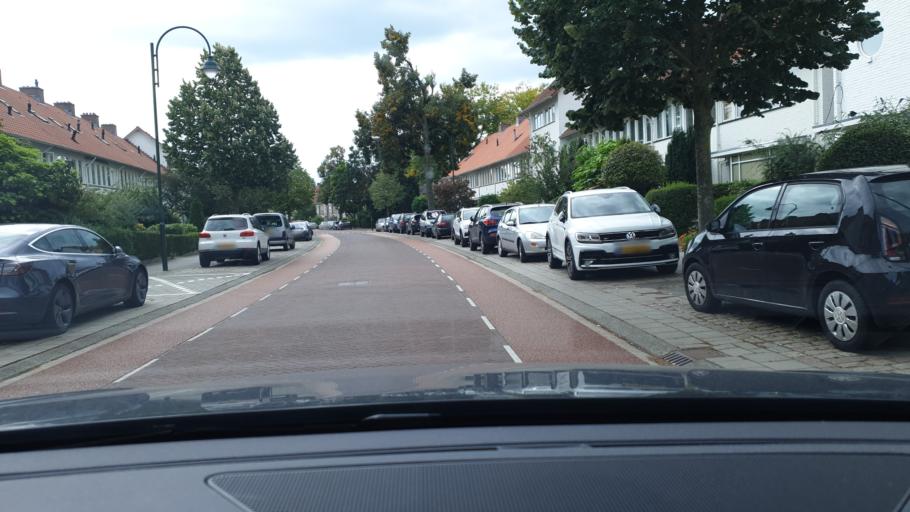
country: NL
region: North Brabant
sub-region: Gemeente Eindhoven
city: Lakerlopen
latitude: 51.4309
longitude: 5.4948
